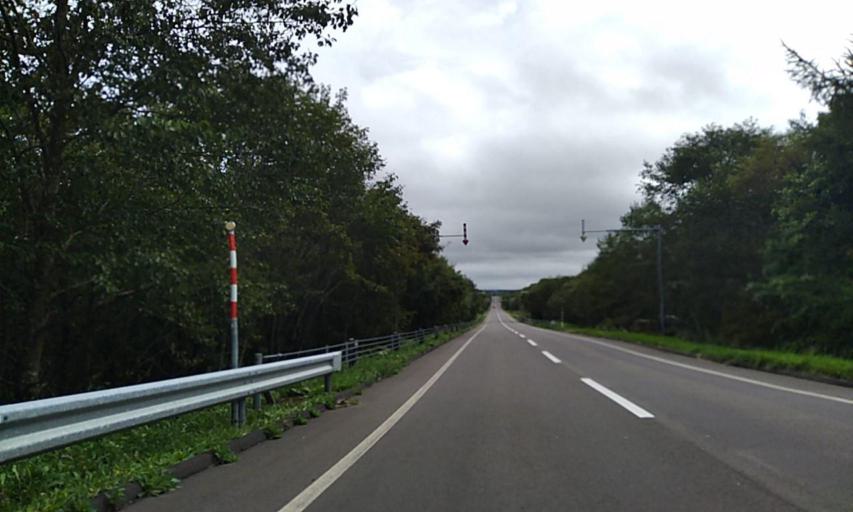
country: JP
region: Hokkaido
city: Nemuro
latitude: 43.2979
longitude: 145.2171
